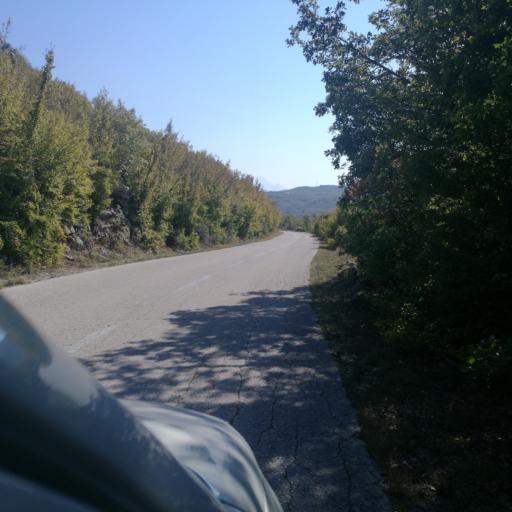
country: HR
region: Splitsko-Dalmatinska
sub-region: Grad Omis
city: Omis
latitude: 43.5215
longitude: 16.7521
